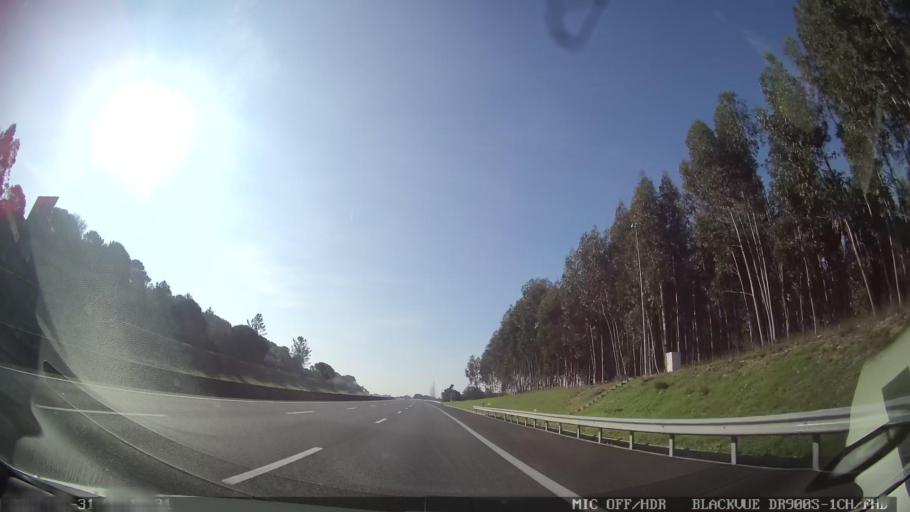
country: PT
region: Santarem
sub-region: Cartaxo
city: Cartaxo
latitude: 39.1953
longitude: -8.8131
